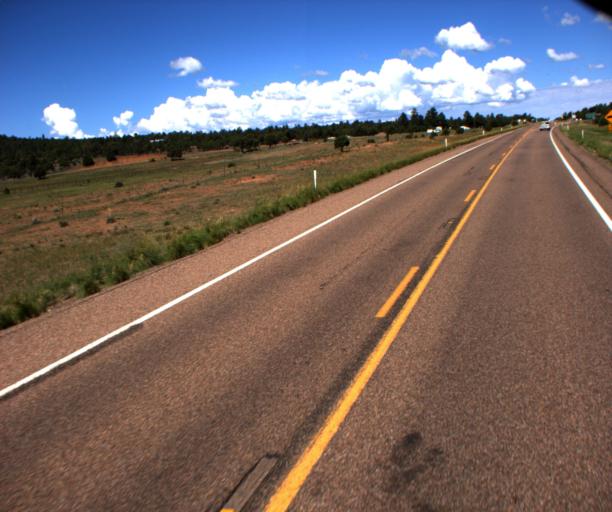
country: US
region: Arizona
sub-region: Navajo County
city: Linden
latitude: 34.3162
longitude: -110.2449
